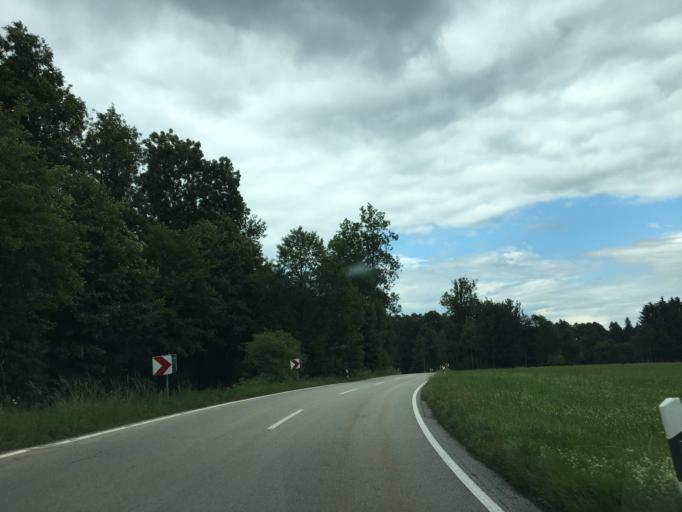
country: DE
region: Bavaria
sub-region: Upper Bavaria
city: Brannenburg
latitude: 47.7489
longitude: 12.0899
